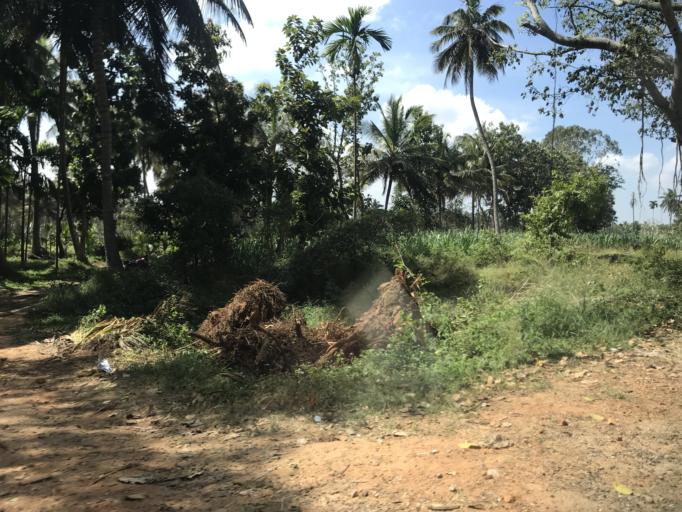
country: IN
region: Karnataka
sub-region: Mandya
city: Shrirangapattana
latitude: 12.4207
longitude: 76.6580
